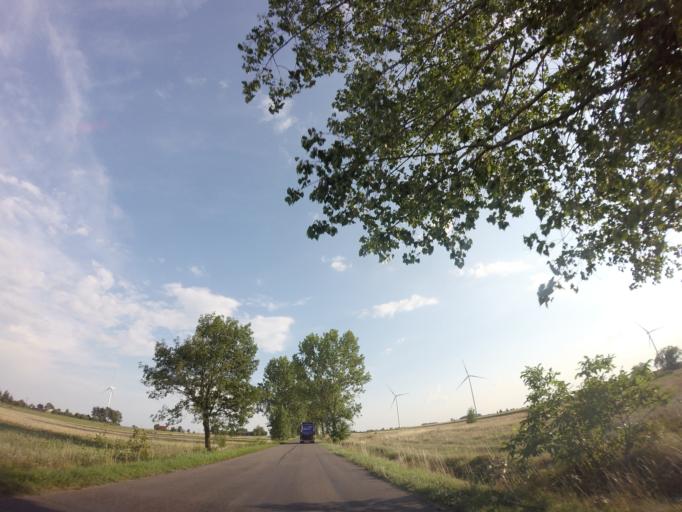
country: PL
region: Lublin Voivodeship
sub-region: Powiat lubartowski
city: Michow
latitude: 51.5105
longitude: 22.3093
